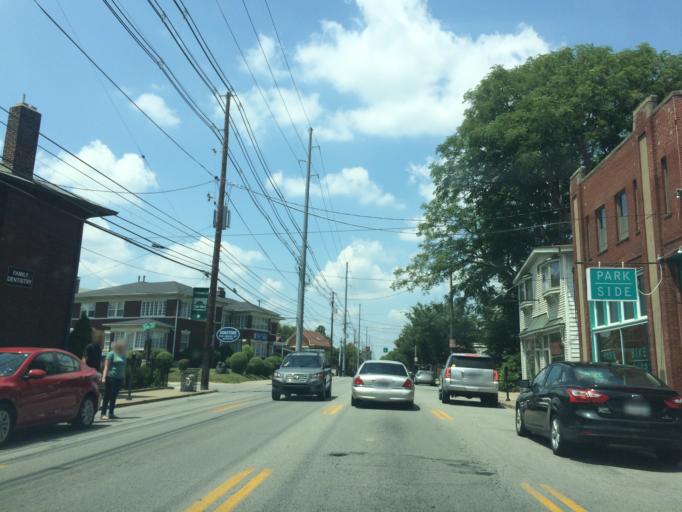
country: US
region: Kentucky
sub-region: Jefferson County
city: Audubon Park
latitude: 38.2335
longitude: -85.7120
